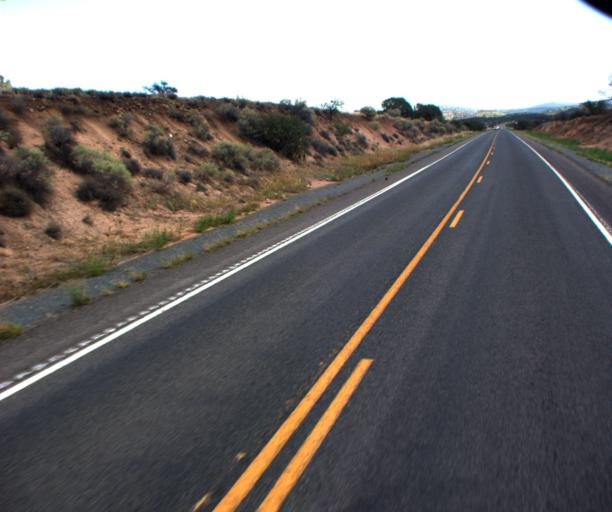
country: US
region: Arizona
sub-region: Yavapai County
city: Camp Verde
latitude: 34.5146
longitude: -112.0152
